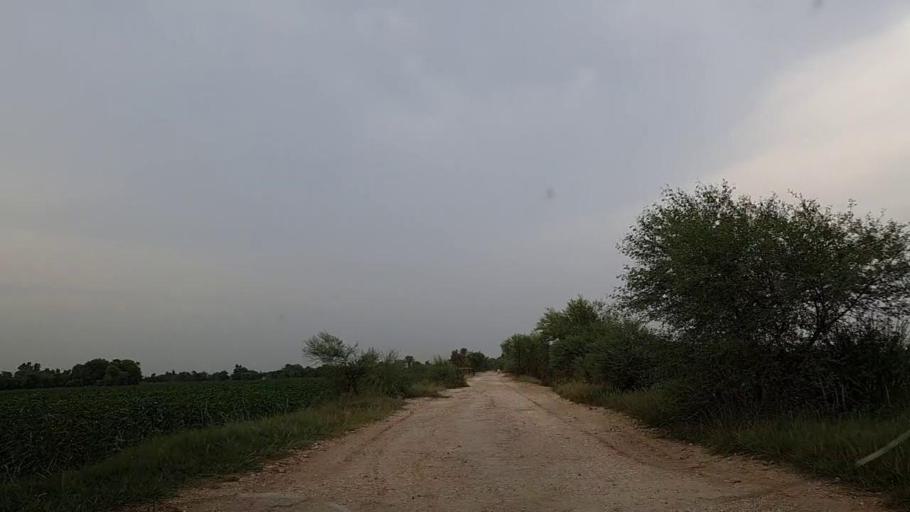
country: PK
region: Sindh
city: Mirpur Mathelo
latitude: 27.8419
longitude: 69.6226
